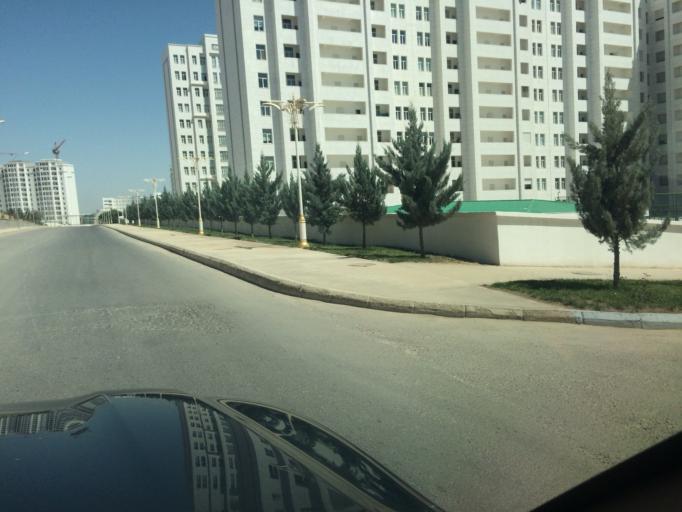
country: TM
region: Ahal
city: Ashgabat
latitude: 37.9338
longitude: 58.3644
